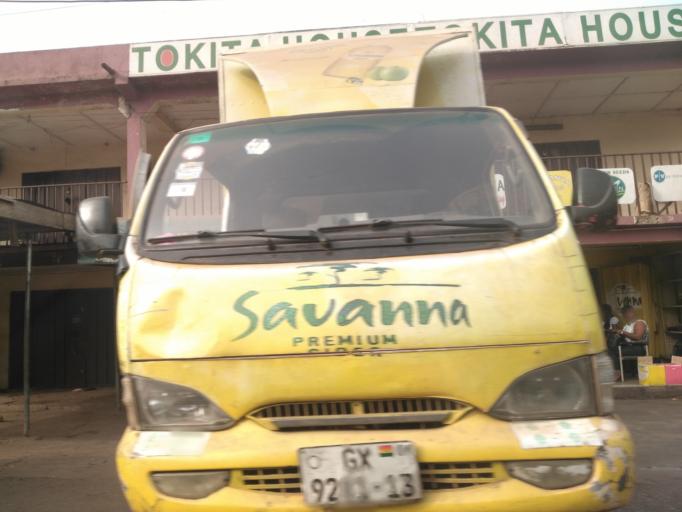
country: GH
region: Ashanti
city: Kumasi
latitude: 6.7069
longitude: -1.6239
